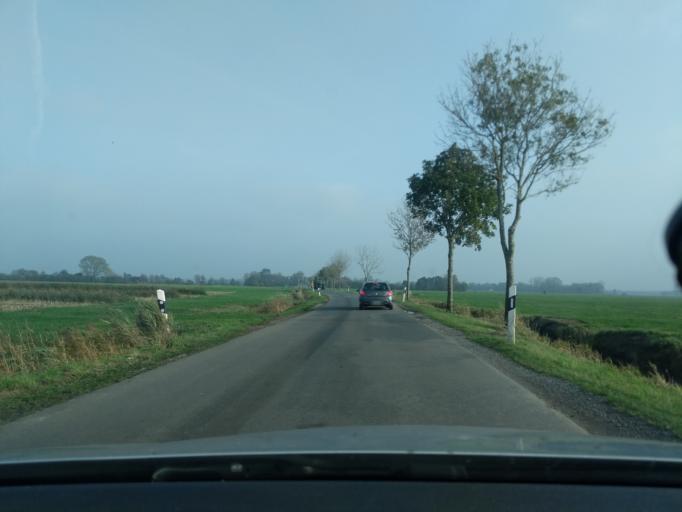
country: DE
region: Lower Saxony
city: Wanna
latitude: 53.7250
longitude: 8.8126
